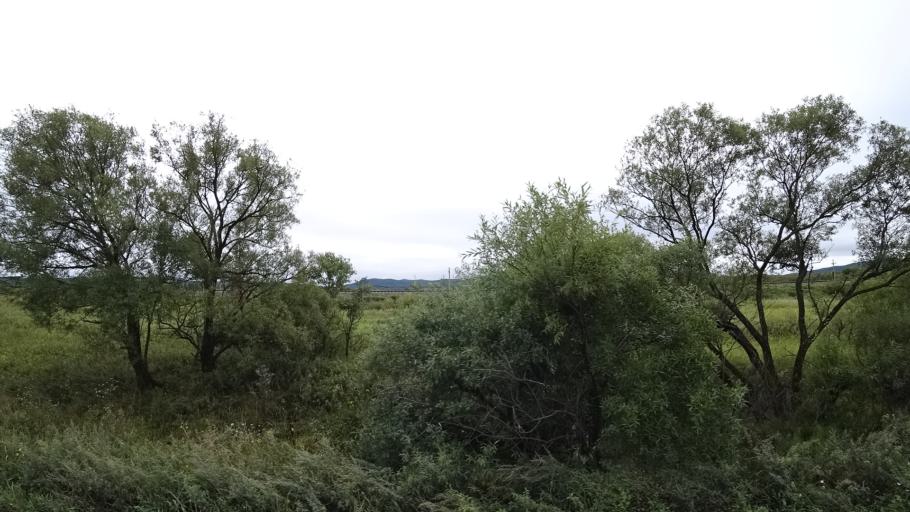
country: RU
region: Primorskiy
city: Monastyrishche
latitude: 44.1774
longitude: 132.4864
